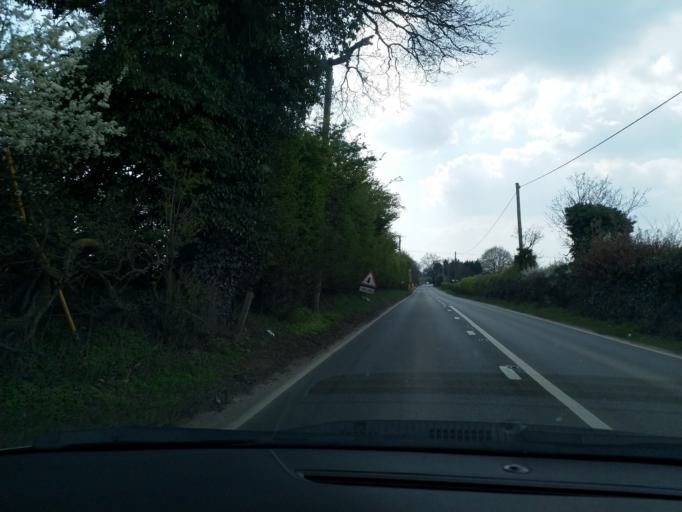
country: GB
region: England
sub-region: Warwickshire
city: Royal Leamington Spa
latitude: 52.3291
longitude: -1.5024
